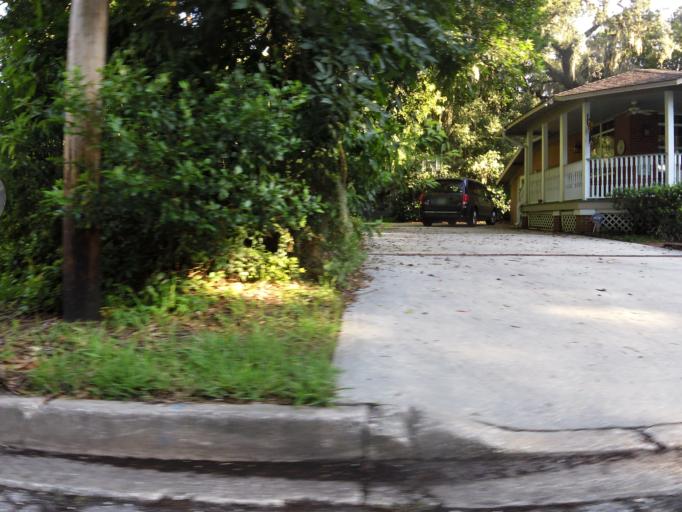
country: US
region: Florida
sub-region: Duval County
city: Jacksonville
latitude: 30.3093
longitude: -81.6314
